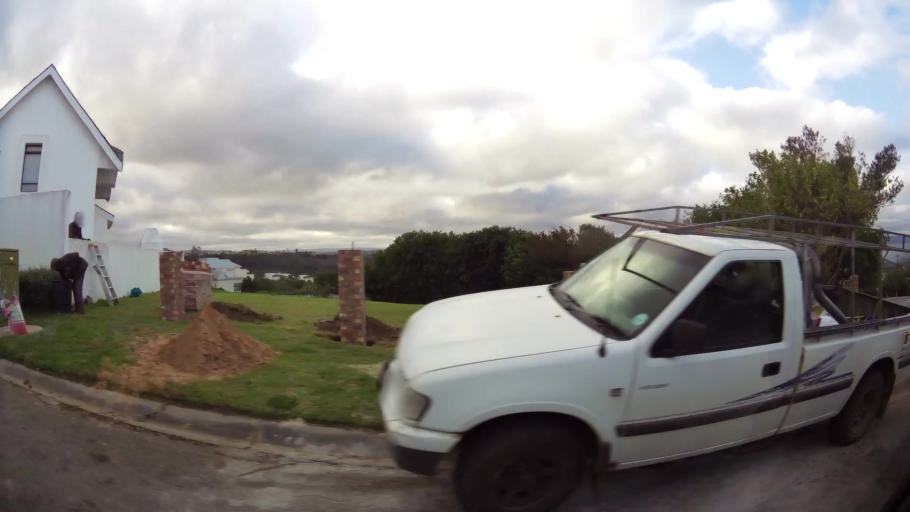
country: ZA
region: Western Cape
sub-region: Eden District Municipality
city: Plettenberg Bay
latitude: -34.0521
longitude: 23.3705
